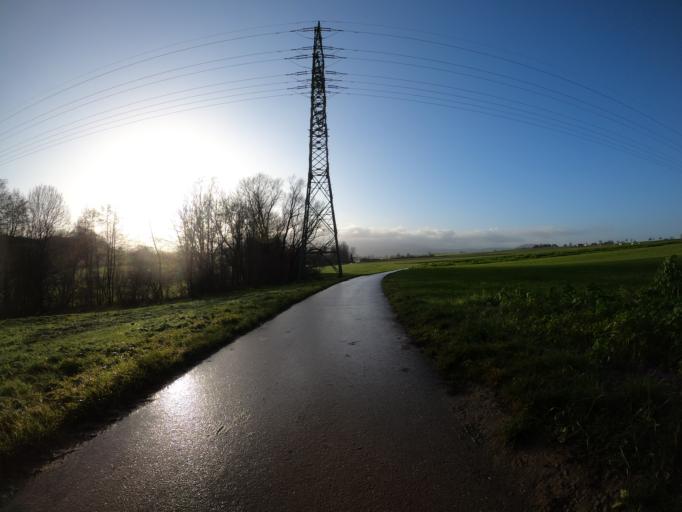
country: DE
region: Baden-Wuerttemberg
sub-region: Regierungsbezirk Stuttgart
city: Heiningen
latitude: 48.6755
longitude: 9.6254
